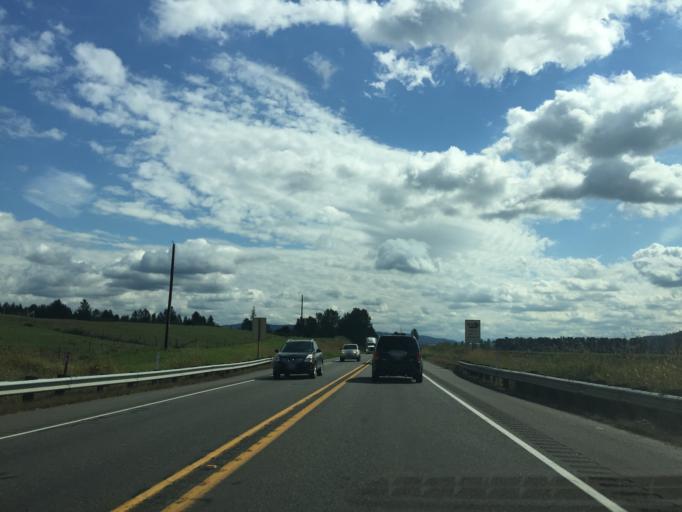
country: US
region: Washington
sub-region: Snohomish County
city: Three Lakes
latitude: 47.8971
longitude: -122.0336
